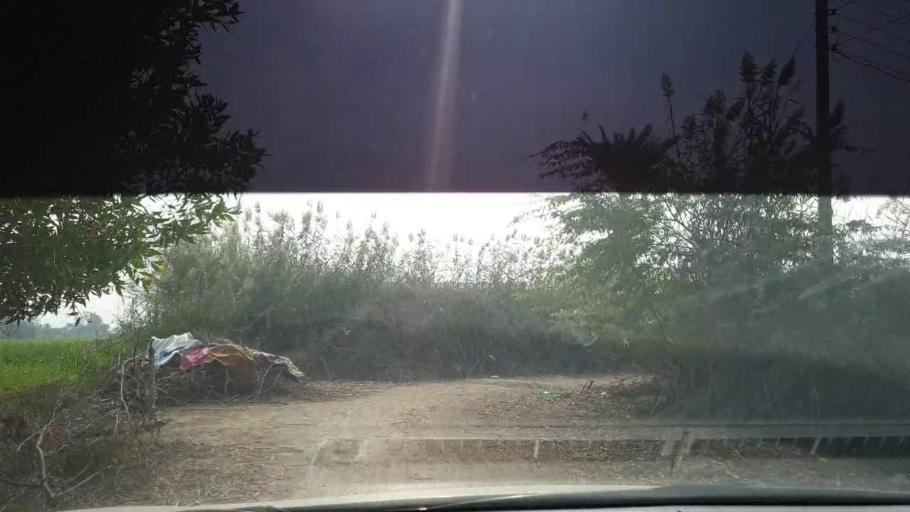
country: PK
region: Sindh
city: Berani
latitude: 25.8412
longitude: 68.8501
